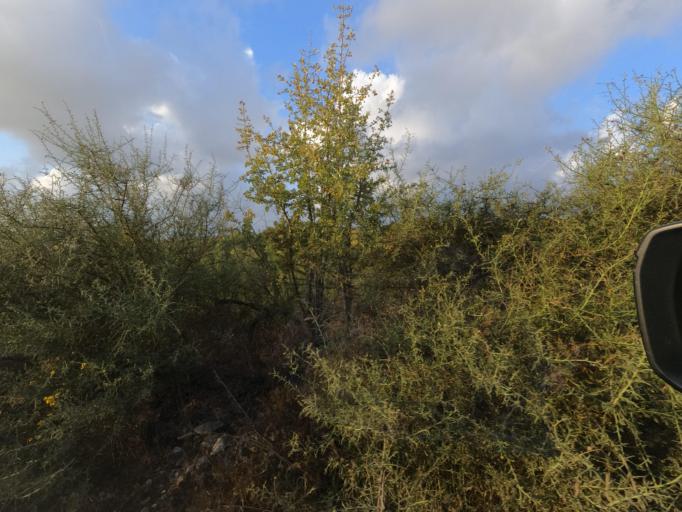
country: CY
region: Pafos
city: Mesogi
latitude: 34.8467
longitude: 32.5315
